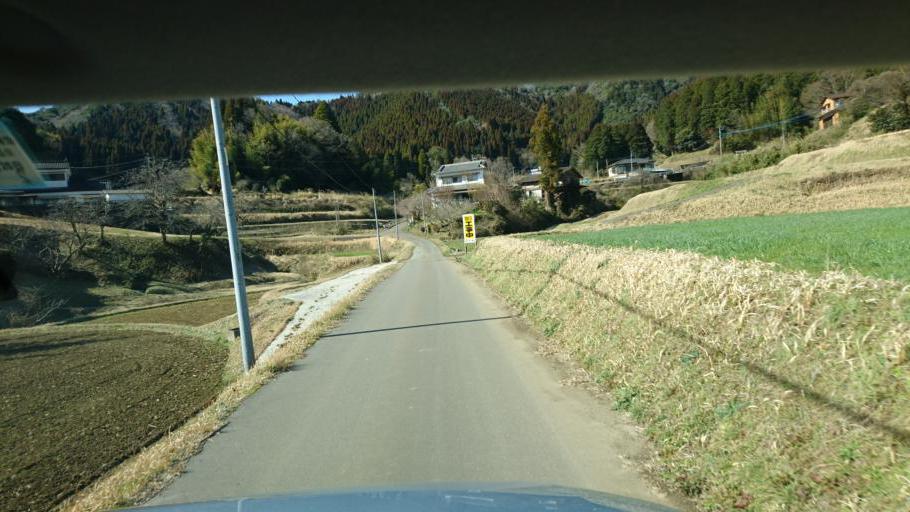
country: JP
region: Oita
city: Takedamachi
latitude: 32.7211
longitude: 131.3057
